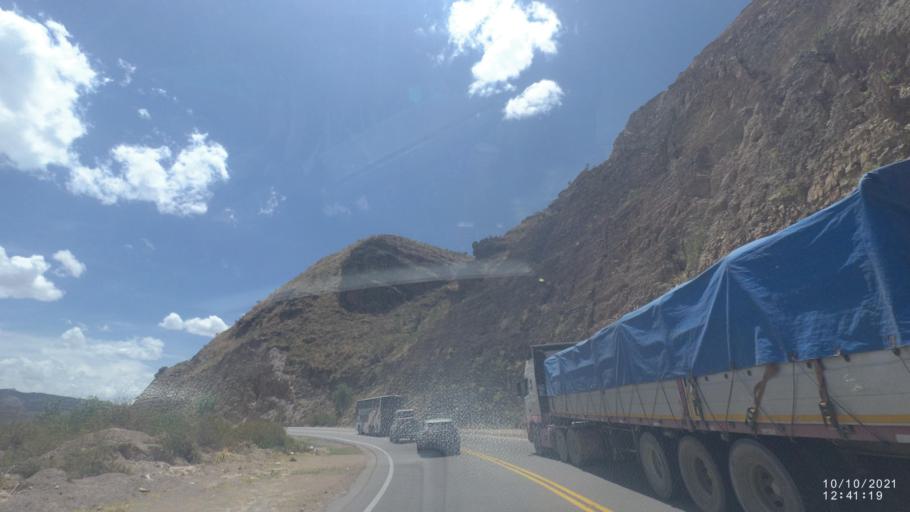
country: BO
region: Cochabamba
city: Irpa Irpa
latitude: -17.6360
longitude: -66.3891
